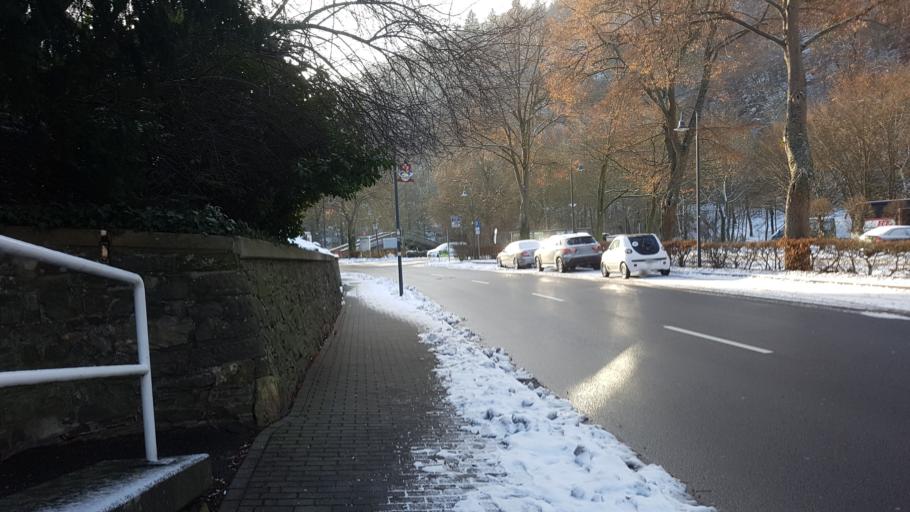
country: DE
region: North Rhine-Westphalia
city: Heimbach
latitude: 50.6346
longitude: 6.4745
